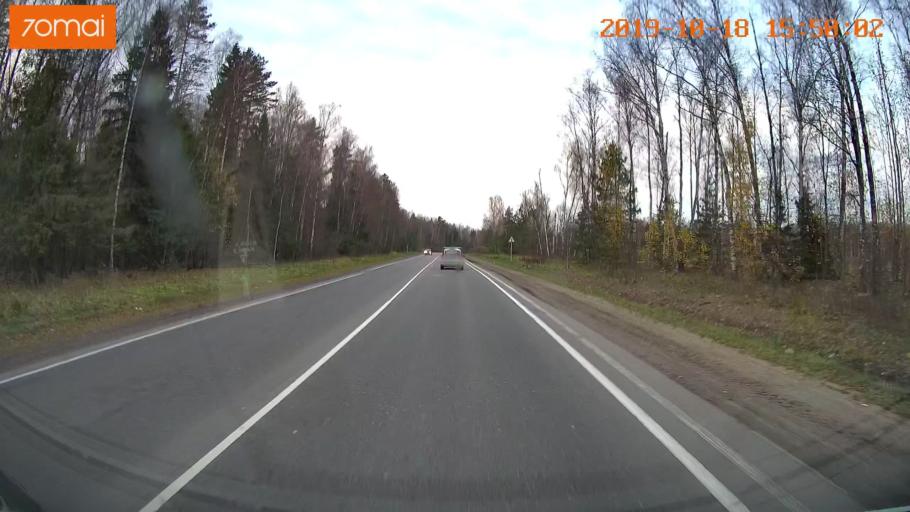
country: RU
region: Vladimir
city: Kommunar
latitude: 56.0289
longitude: 40.5661
